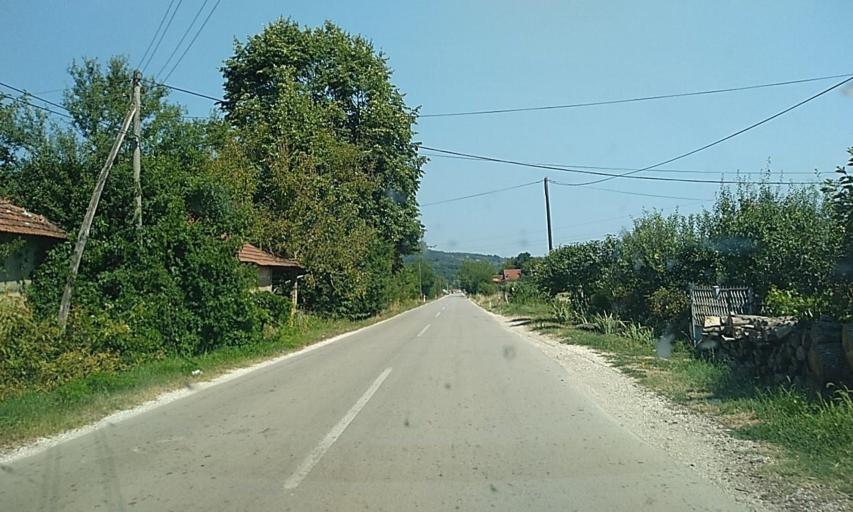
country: RS
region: Central Serbia
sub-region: Pcinjski Okrug
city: Vladicin Han
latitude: 42.6633
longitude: 22.0460
